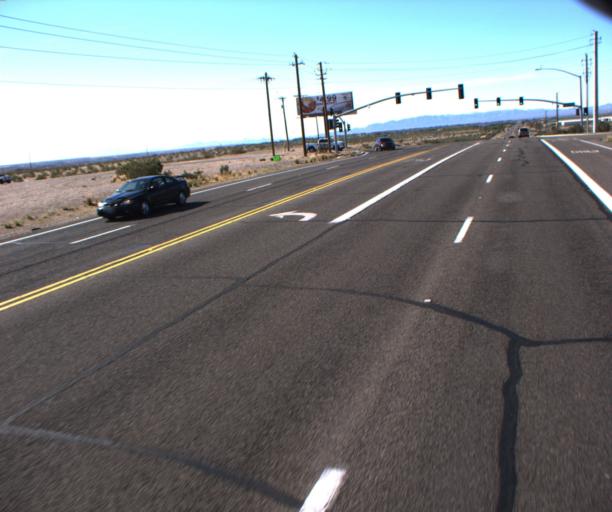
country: US
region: Arizona
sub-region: Mohave County
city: Mohave Valley
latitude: 34.9832
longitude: -114.5981
